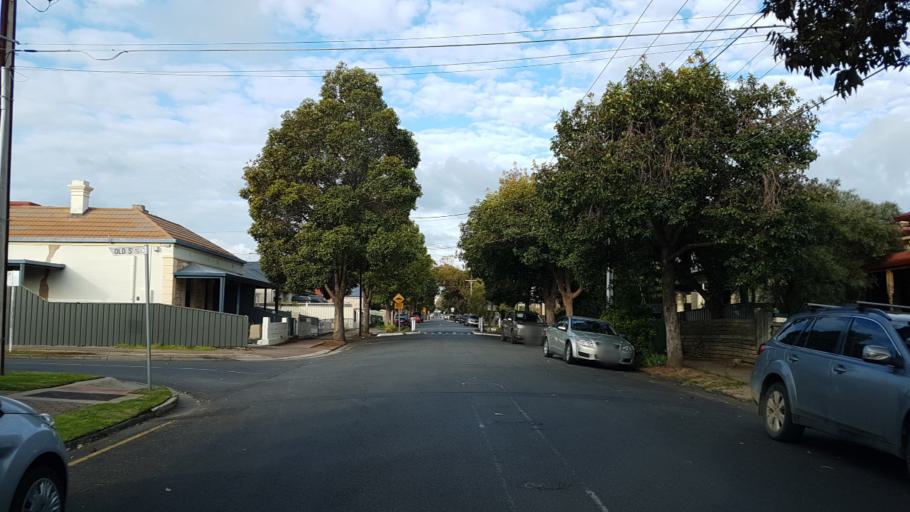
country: AU
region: South Australia
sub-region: Prospect
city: Prospect
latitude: -34.8889
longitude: 138.5973
